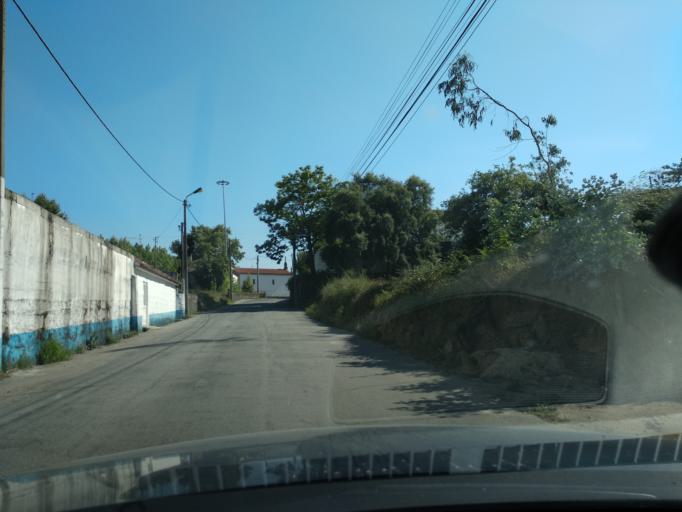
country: PT
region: Porto
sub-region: Paredes
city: Rebordosa
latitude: 41.2244
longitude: -8.4143
